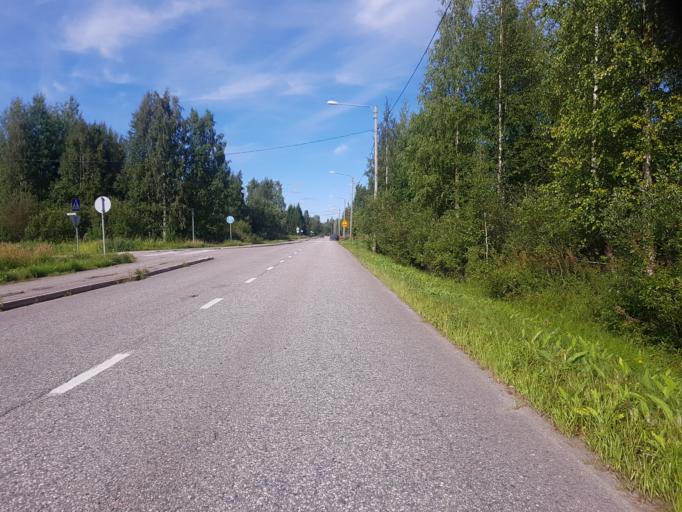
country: FI
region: Kainuu
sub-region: Kehys-Kainuu
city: Kuhmo
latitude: 64.1225
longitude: 29.5455
